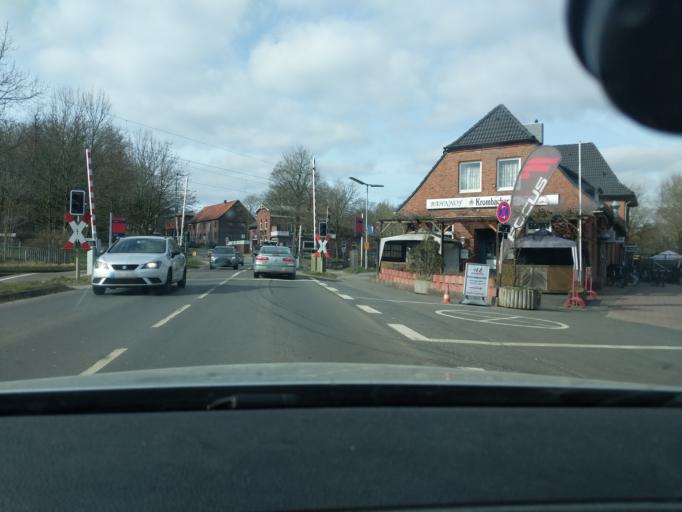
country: DE
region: Lower Saxony
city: Dollern
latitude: 53.5453
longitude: 9.5586
